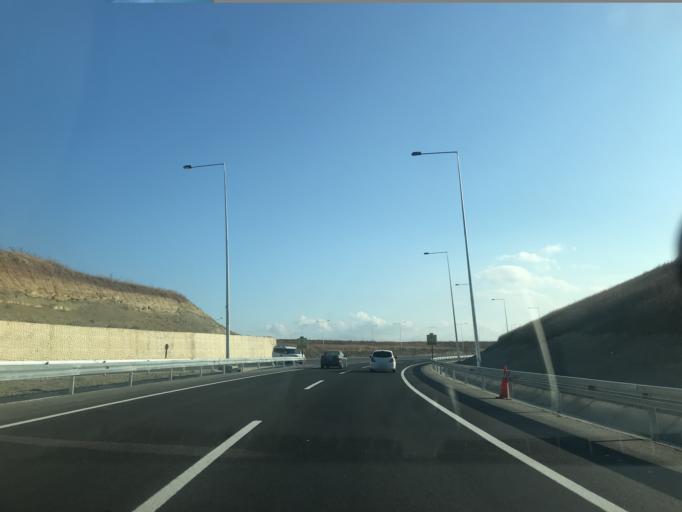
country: TR
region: Istanbul
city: Silivri
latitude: 41.1224
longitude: 28.1920
